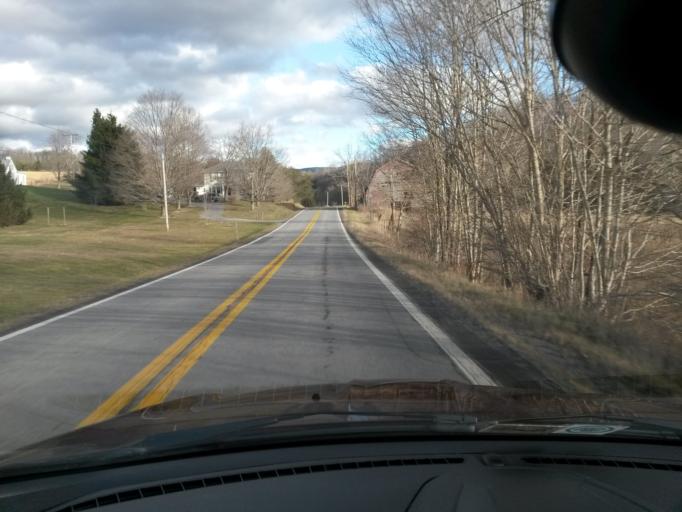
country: US
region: West Virginia
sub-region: Monroe County
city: Union
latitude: 37.4776
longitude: -80.6488
